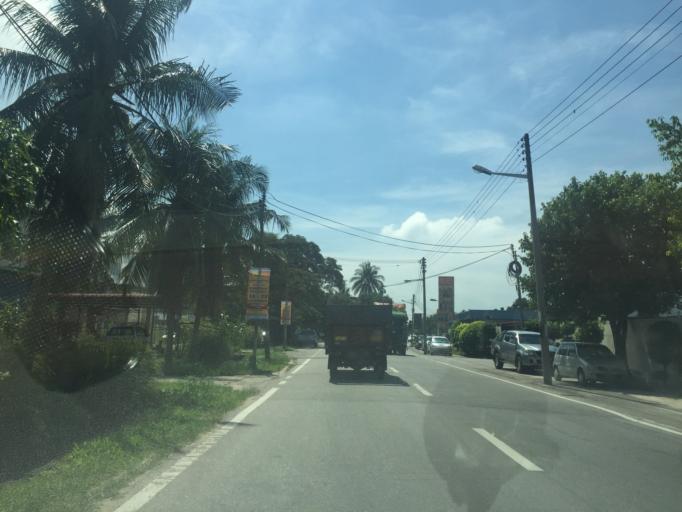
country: MY
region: Penang
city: Permatang Kuching
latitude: 5.4429
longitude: 100.3974
